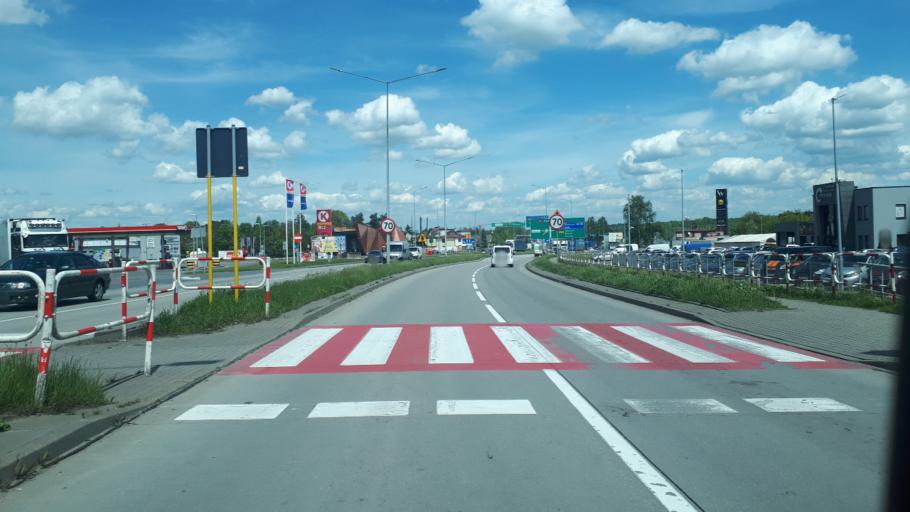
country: PL
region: Silesian Voivodeship
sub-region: Zory
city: Zory
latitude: 50.0425
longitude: 18.6990
